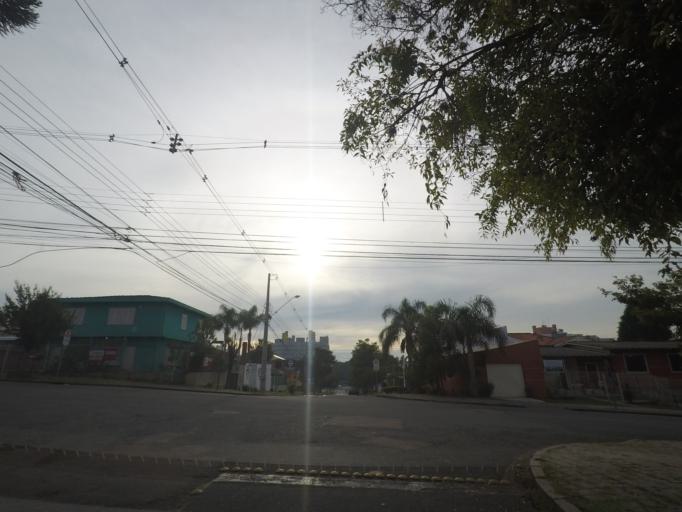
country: BR
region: Parana
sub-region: Curitiba
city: Curitiba
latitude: -25.4358
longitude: -49.2948
